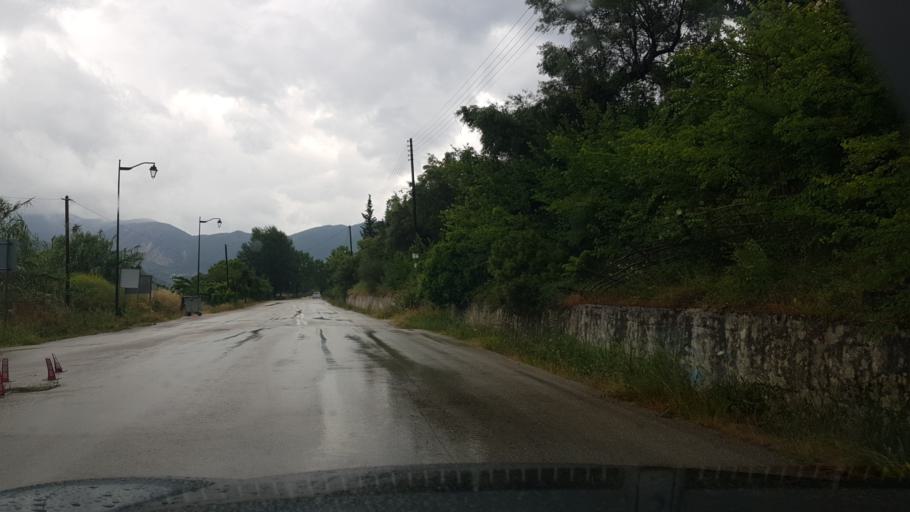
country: GR
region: Ionian Islands
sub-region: Lefkada
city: Nidri
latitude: 38.6290
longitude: 20.6117
